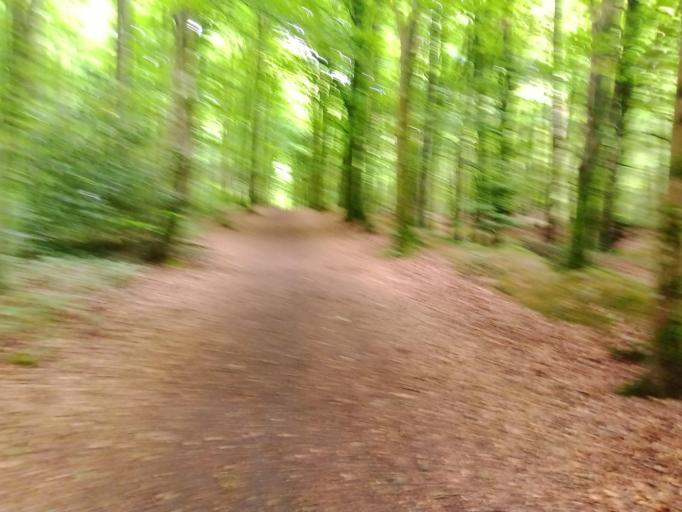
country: IE
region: Leinster
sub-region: Laois
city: Stradbally
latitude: 53.0037
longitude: -7.1233
